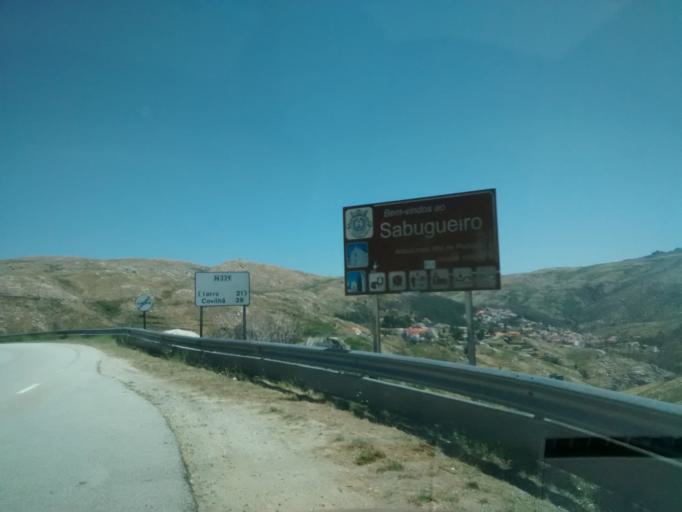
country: PT
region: Guarda
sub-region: Seia
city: Seia
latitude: 40.4041
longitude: -7.6591
